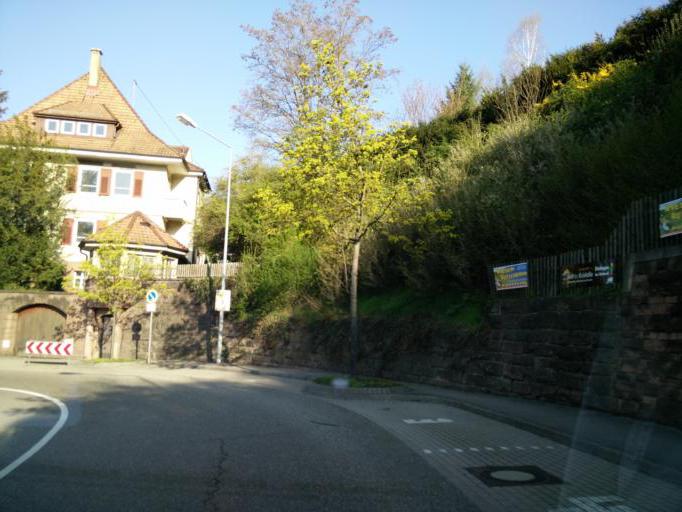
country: DE
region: Baden-Wuerttemberg
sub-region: Karlsruhe Region
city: Calw
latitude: 48.7144
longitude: 8.7478
